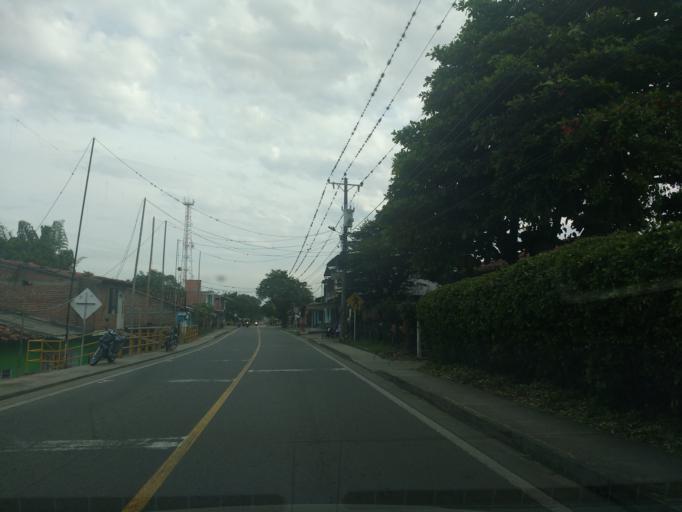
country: CO
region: Cauca
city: Miranda
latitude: 3.2831
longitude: -76.2240
